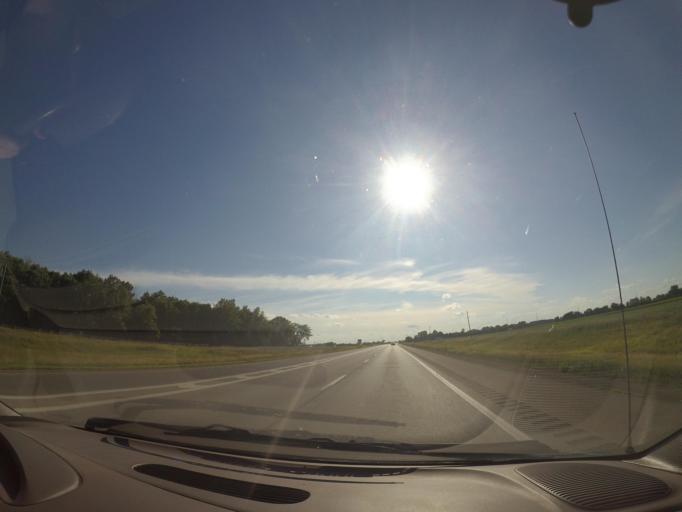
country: US
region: Ohio
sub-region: Henry County
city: Napoleon
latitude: 41.4169
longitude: -84.0694
